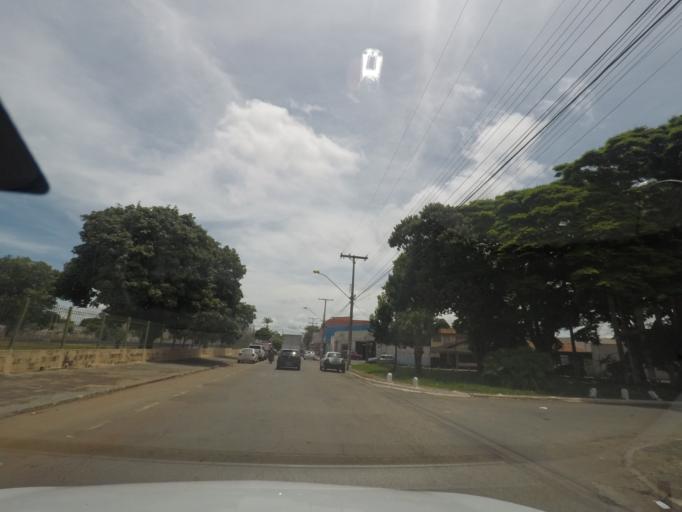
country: BR
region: Goias
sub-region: Goiania
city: Goiania
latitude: -16.6901
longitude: -49.3099
